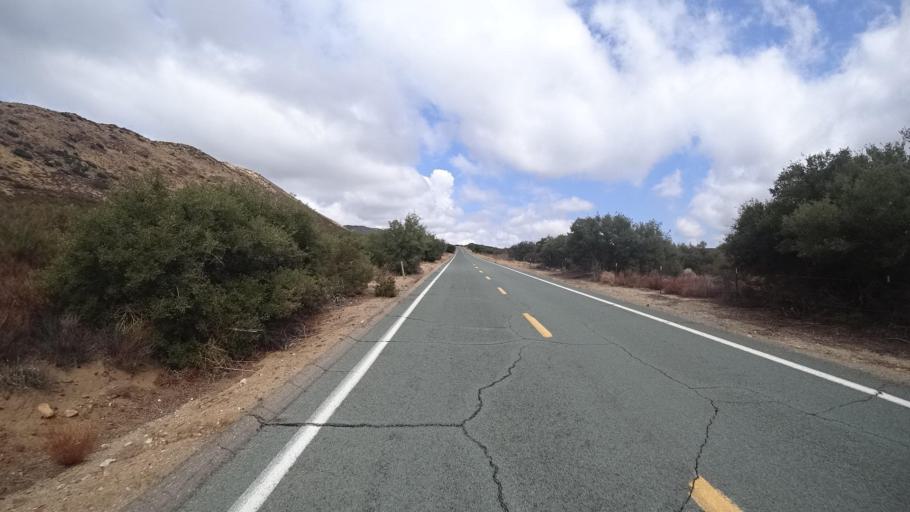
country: US
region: California
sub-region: San Diego County
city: Pine Valley
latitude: 32.7297
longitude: -116.4589
